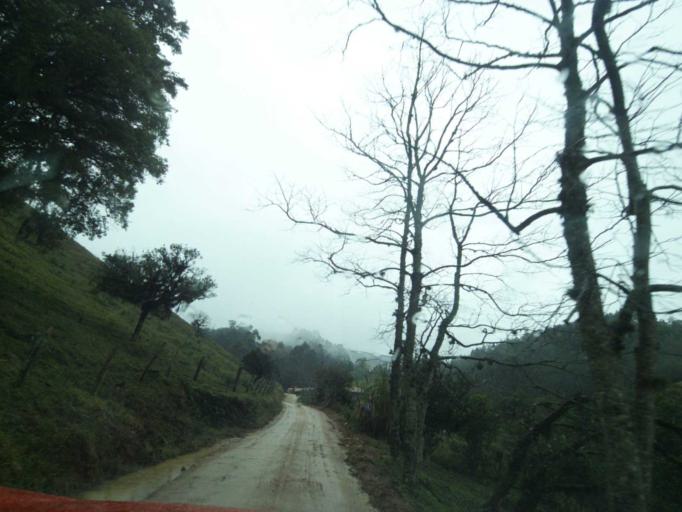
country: BR
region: Santa Catarina
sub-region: Anitapolis
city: Anitapolis
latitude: -27.8971
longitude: -49.1942
